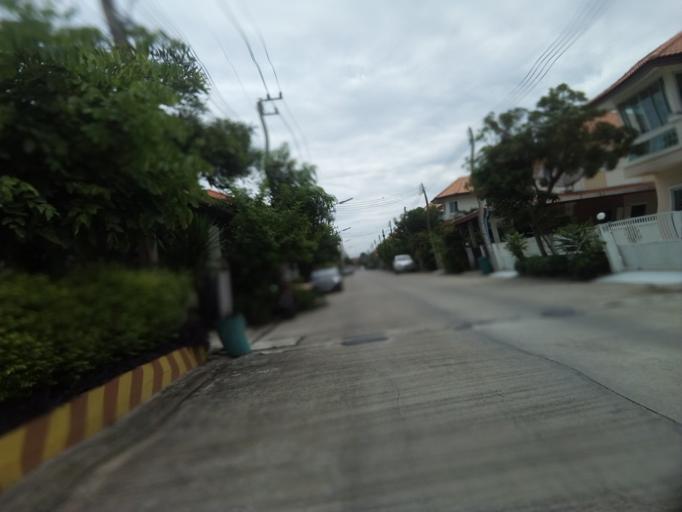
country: TH
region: Pathum Thani
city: Ban Rangsit
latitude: 14.0502
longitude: 100.8348
